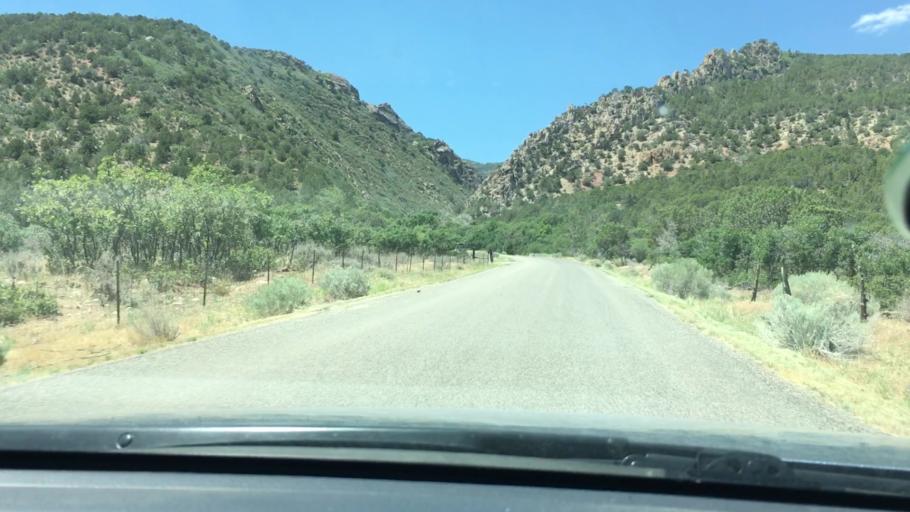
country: US
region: Utah
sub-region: Sanpete County
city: Moroni
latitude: 39.5558
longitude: -111.6581
